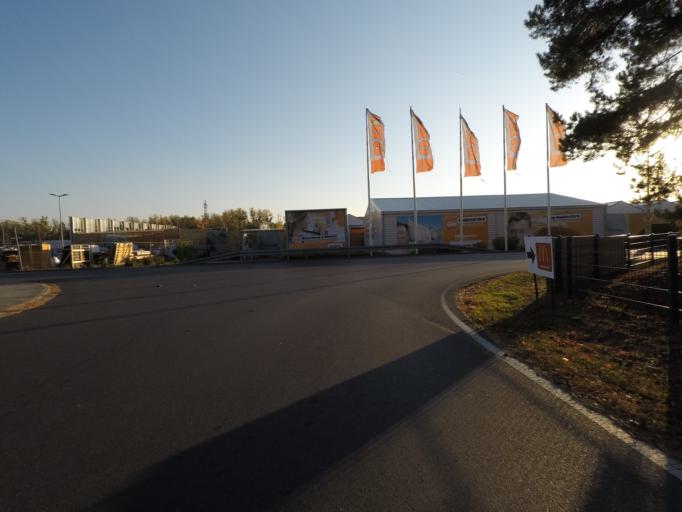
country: DE
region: Brandenburg
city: Melchow
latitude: 52.8409
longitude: 13.6970
